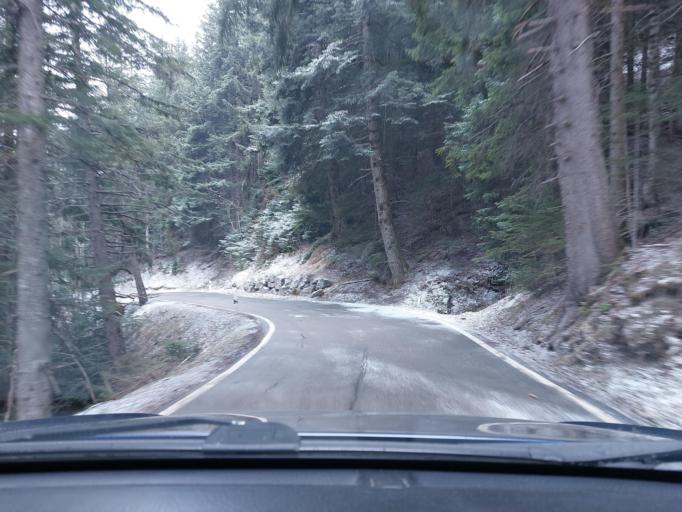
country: CH
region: Valais
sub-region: Sion District
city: Saviese
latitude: 46.2885
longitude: 7.3241
